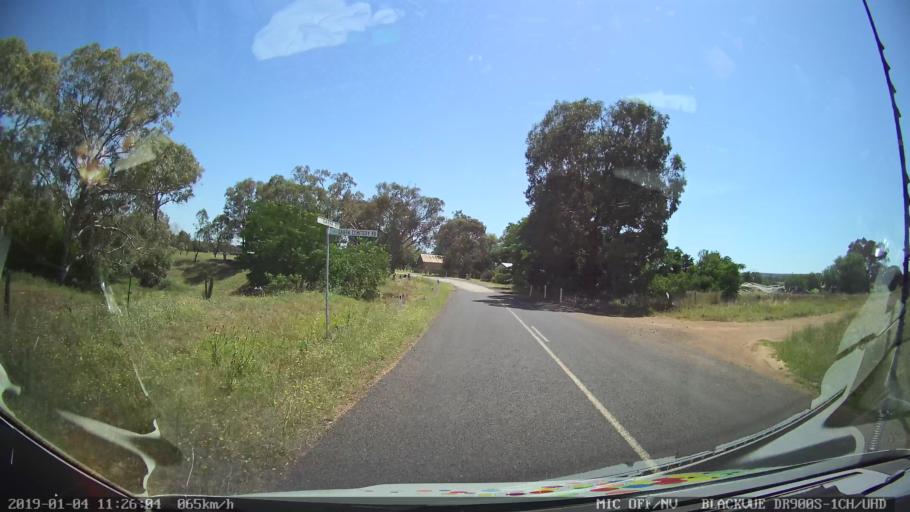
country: AU
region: New South Wales
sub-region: Cabonne
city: Molong
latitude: -33.1178
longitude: 148.7550
